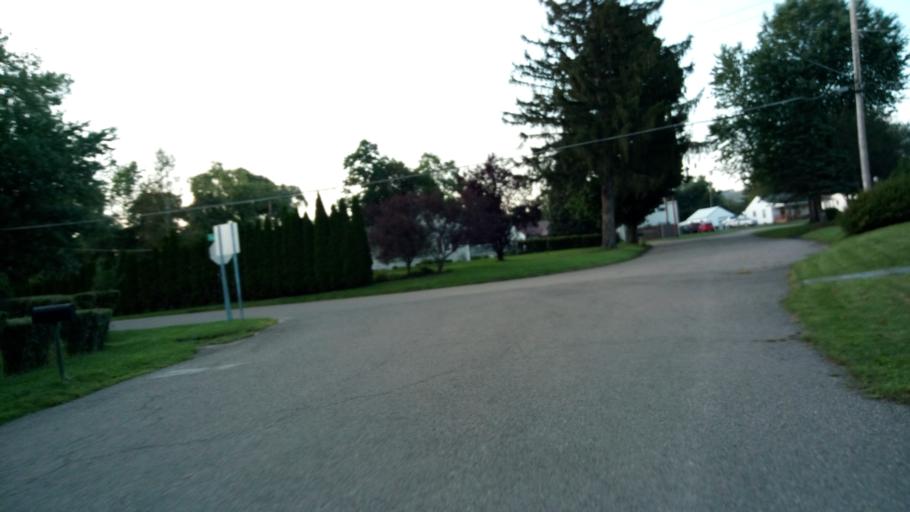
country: US
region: New York
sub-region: Chemung County
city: Elmira
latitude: 42.0712
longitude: -76.7909
